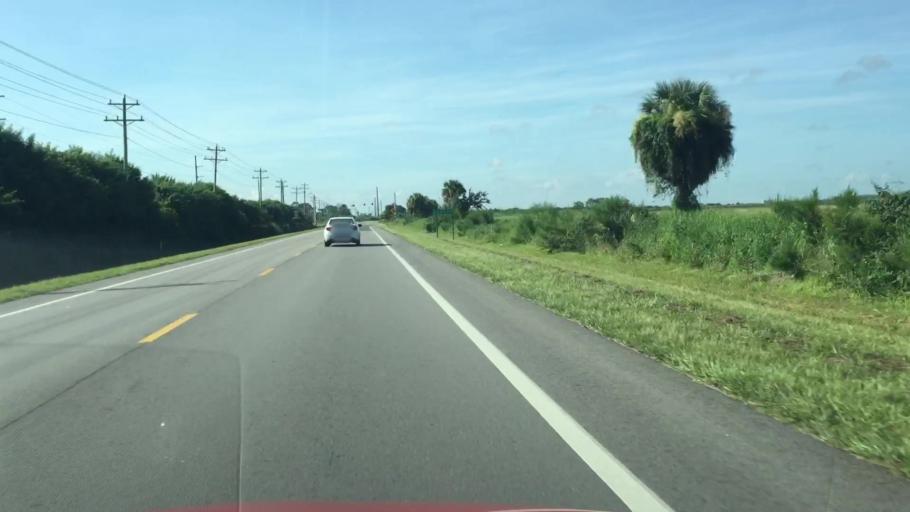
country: US
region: Florida
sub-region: Collier County
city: Immokalee
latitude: 26.3780
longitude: -81.4171
